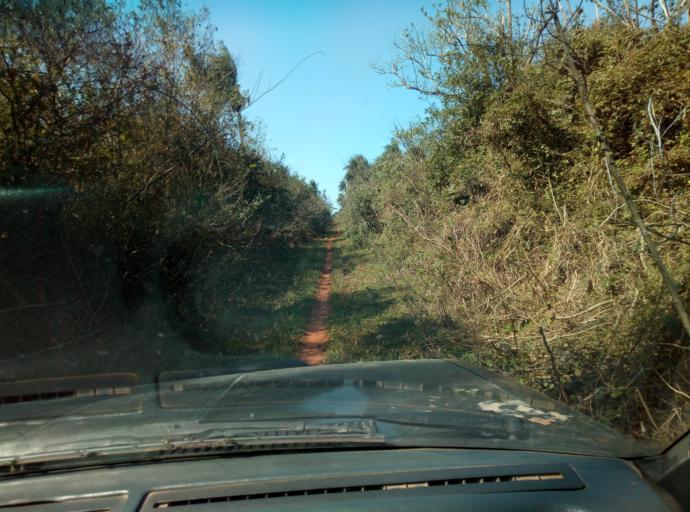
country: PY
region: Caaguazu
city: Doctor Cecilio Baez
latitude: -25.1793
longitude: -56.2196
